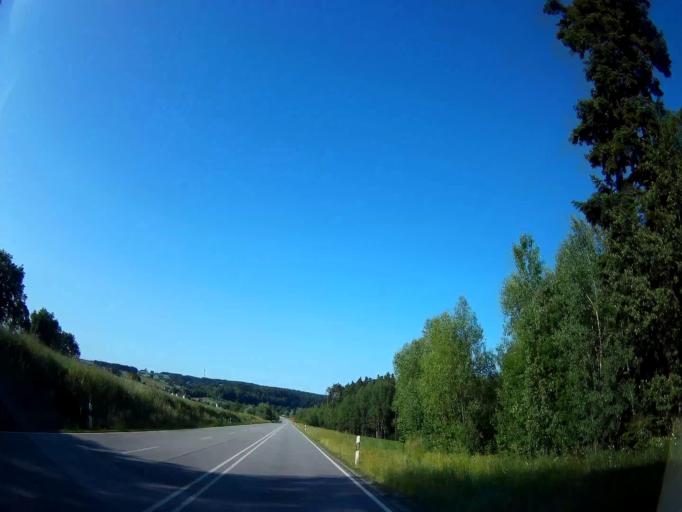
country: DE
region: Bavaria
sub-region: Lower Bavaria
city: Malgersdorf
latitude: 48.5235
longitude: 12.7490
